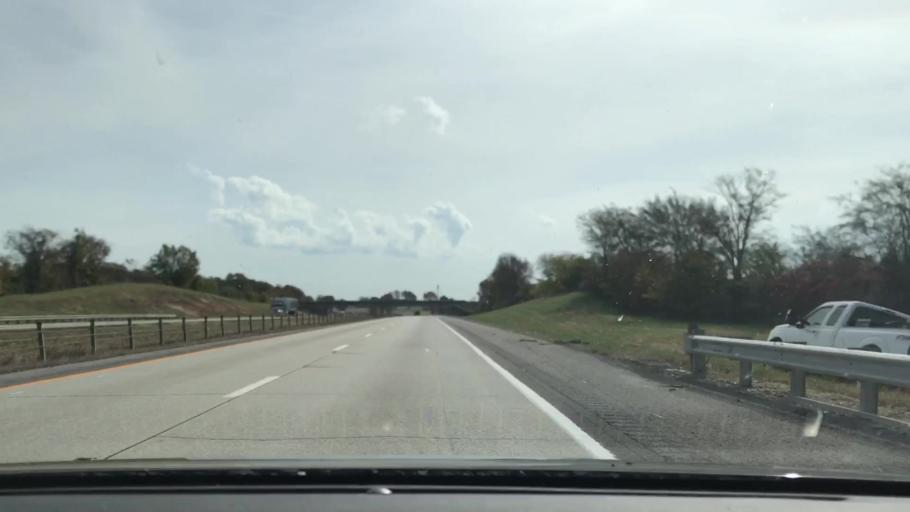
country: US
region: Kentucky
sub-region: Trigg County
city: Cadiz
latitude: 36.8323
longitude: -87.6639
